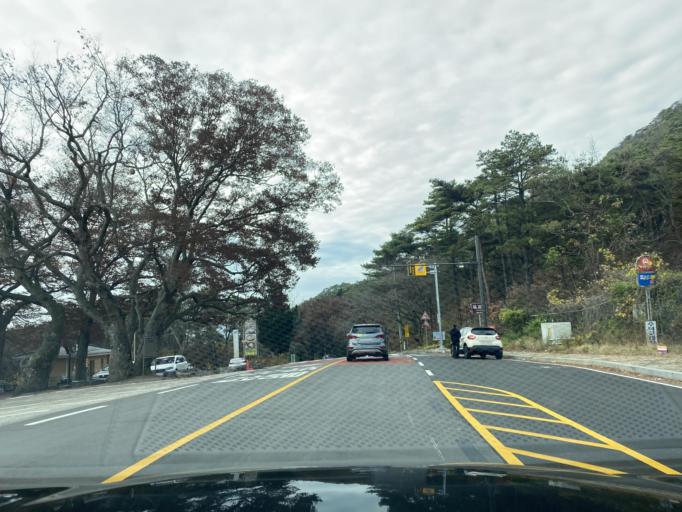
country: KR
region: Chungcheongnam-do
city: Hongsung
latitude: 36.6614
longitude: 126.6309
